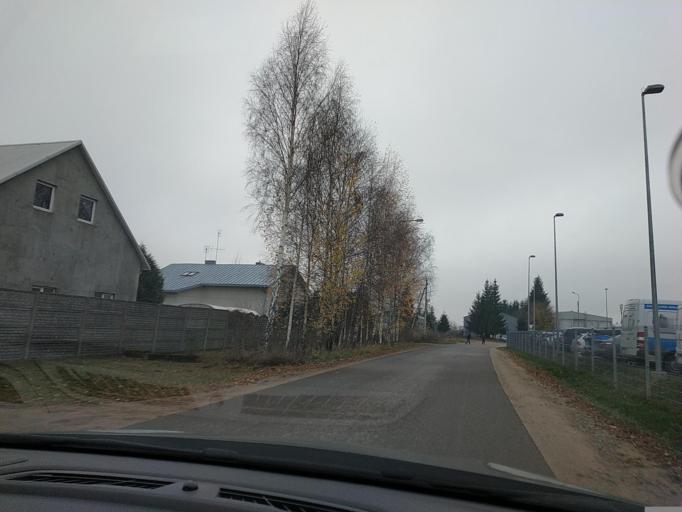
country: LT
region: Vilnius County
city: Rasos
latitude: 54.6416
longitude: 25.3336
